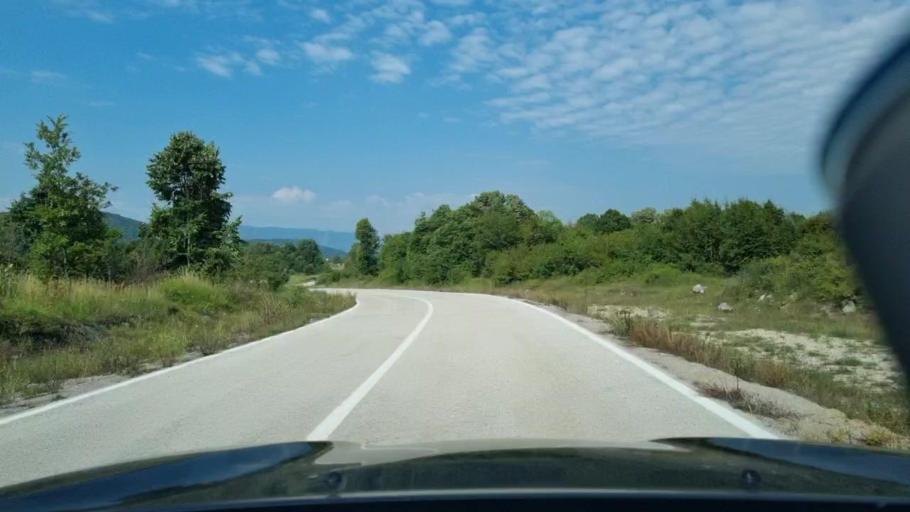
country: BA
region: Federation of Bosnia and Herzegovina
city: Ostrozac
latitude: 44.8945
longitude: 15.9721
